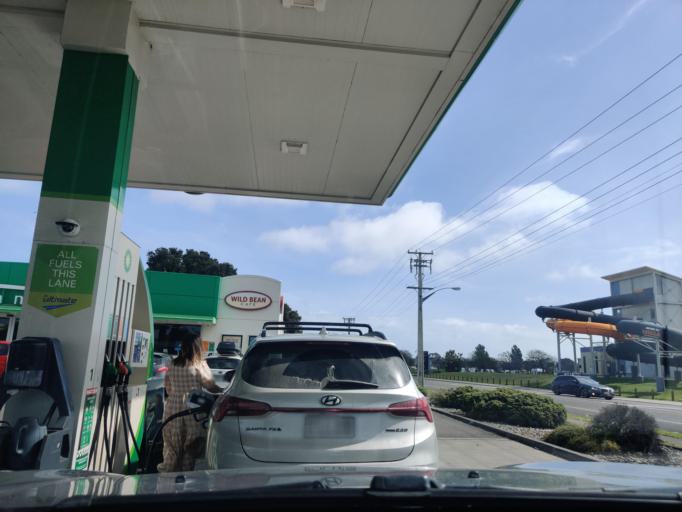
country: NZ
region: Manawatu-Wanganui
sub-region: Wanganui District
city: Wanganui
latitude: -39.9301
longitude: 175.0318
